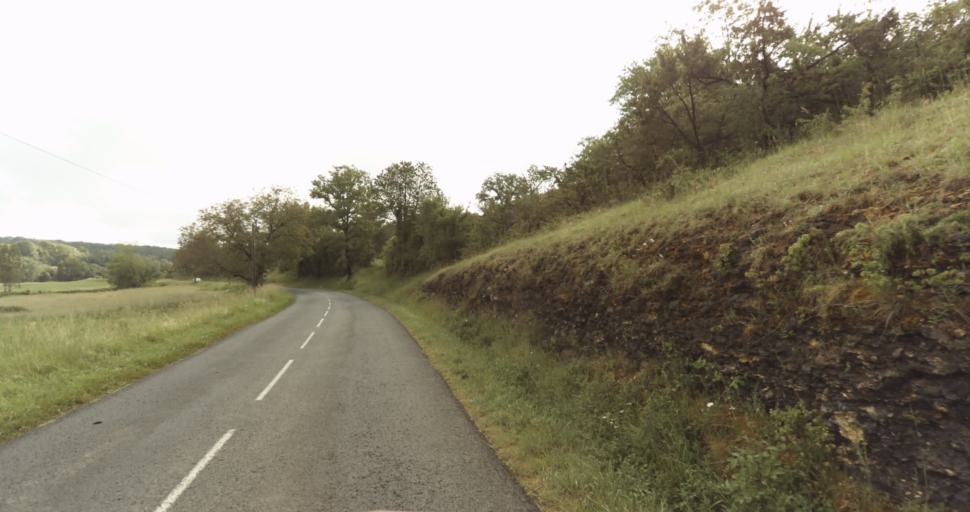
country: FR
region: Aquitaine
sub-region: Departement de la Dordogne
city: Lalinde
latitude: 44.9297
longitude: 0.7641
